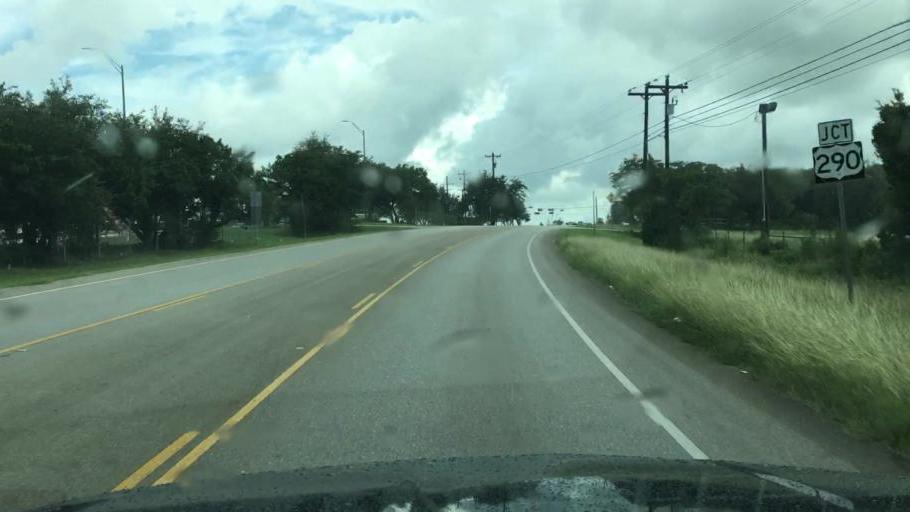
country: US
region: Texas
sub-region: Travis County
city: Bee Cave
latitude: 30.2063
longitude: -97.9729
